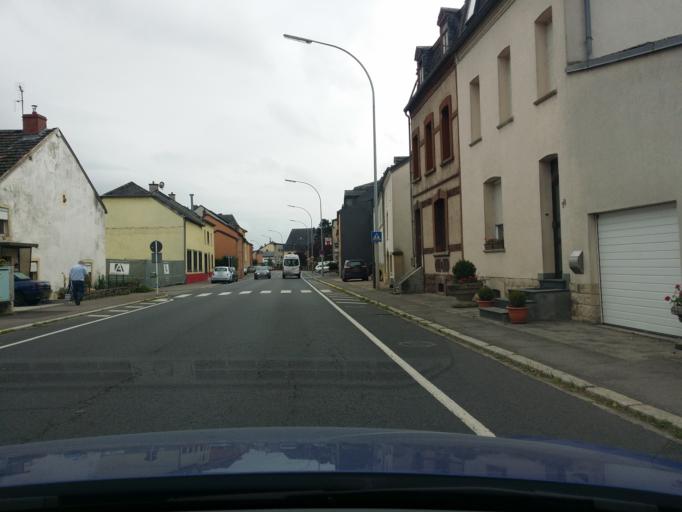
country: LU
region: Luxembourg
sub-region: Canton de Mersch
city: Lintgen
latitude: 49.7225
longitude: 6.1244
